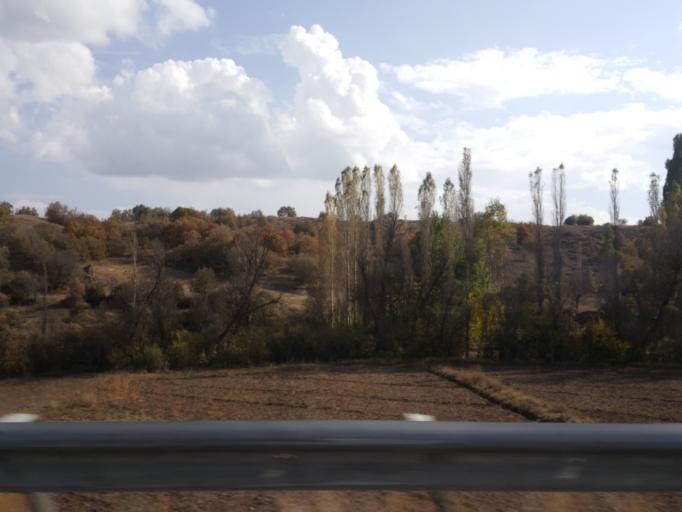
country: TR
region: Corum
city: Alaca
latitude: 40.3194
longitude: 34.6904
